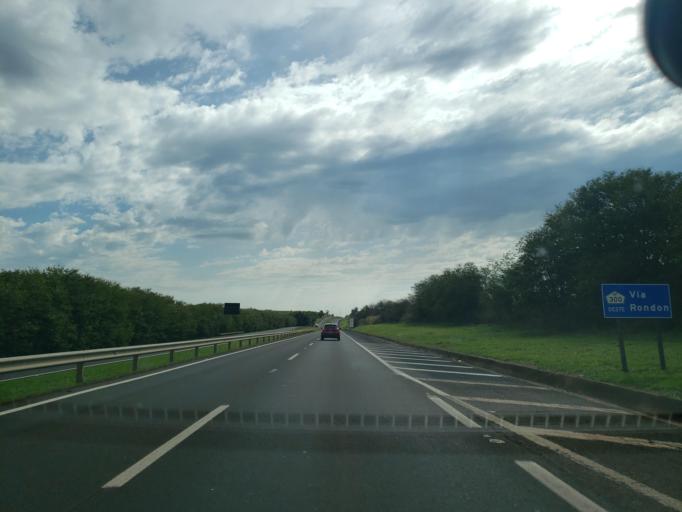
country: BR
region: Sao Paulo
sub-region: Cafelandia
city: Cafelandia
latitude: -21.8031
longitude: -49.6370
